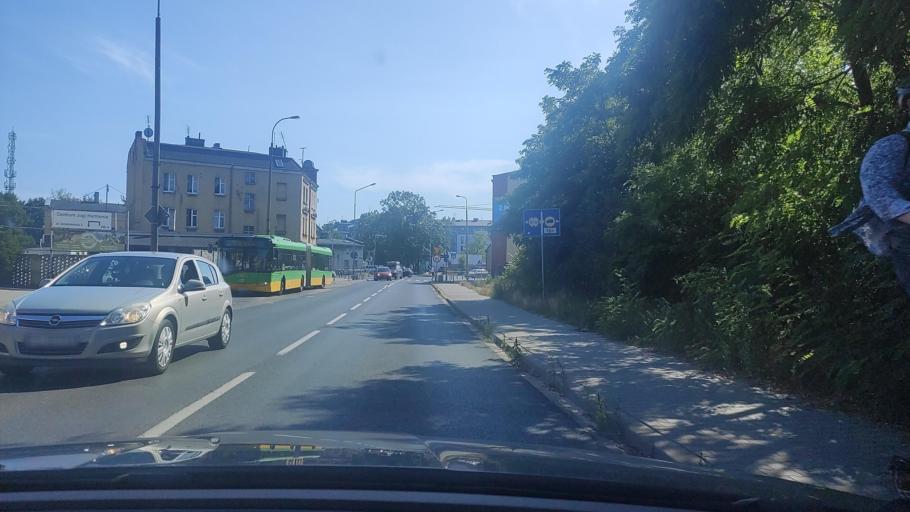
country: PL
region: Greater Poland Voivodeship
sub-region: Powiat poznanski
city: Czerwonak
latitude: 52.4232
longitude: 16.9767
